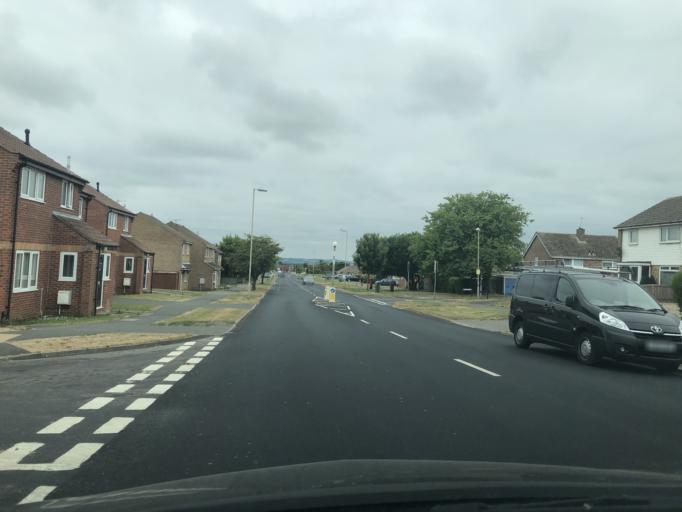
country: GB
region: England
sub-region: North Yorkshire
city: Scarborough
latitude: 54.2440
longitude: -0.3879
